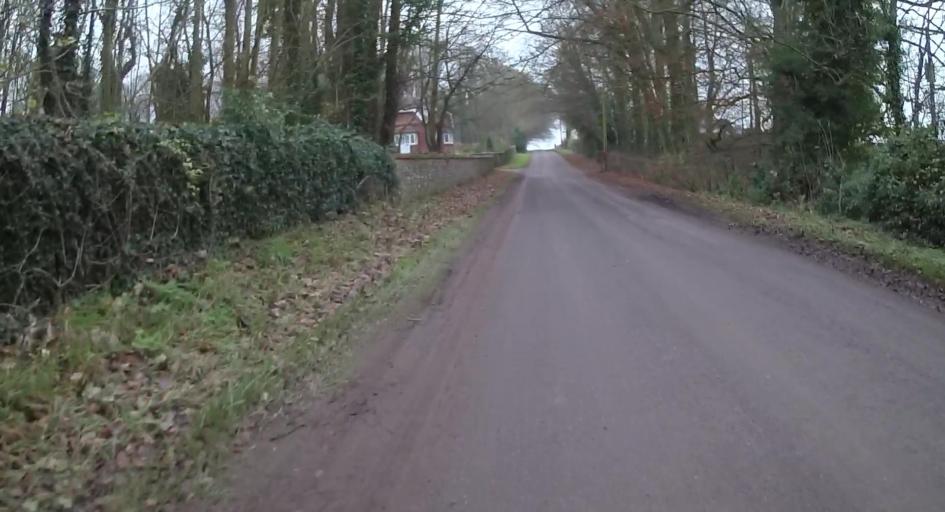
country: GB
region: England
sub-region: Hampshire
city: Kings Worthy
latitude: 51.1273
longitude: -1.2115
